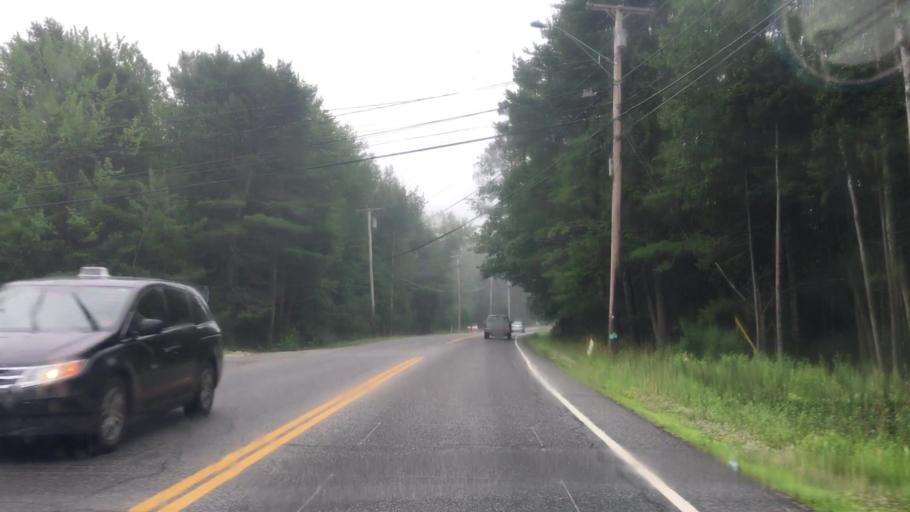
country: US
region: Maine
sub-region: Lincoln County
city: Boothbay
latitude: 43.9147
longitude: -69.6149
